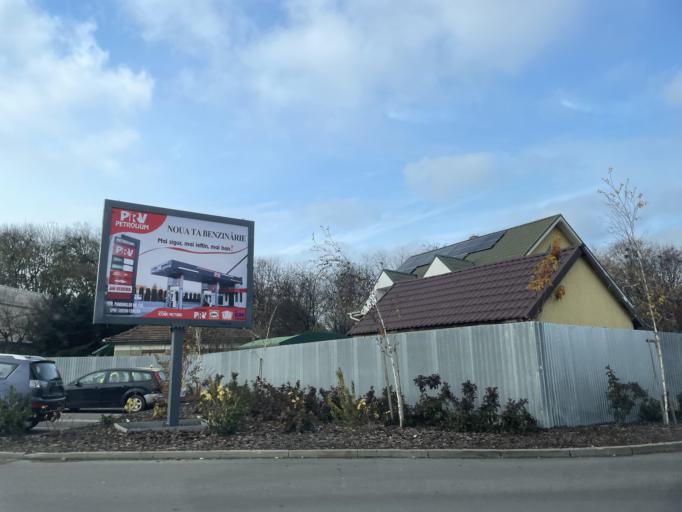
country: RO
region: Mures
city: Reghin-Sat
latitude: 46.7788
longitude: 24.7119
